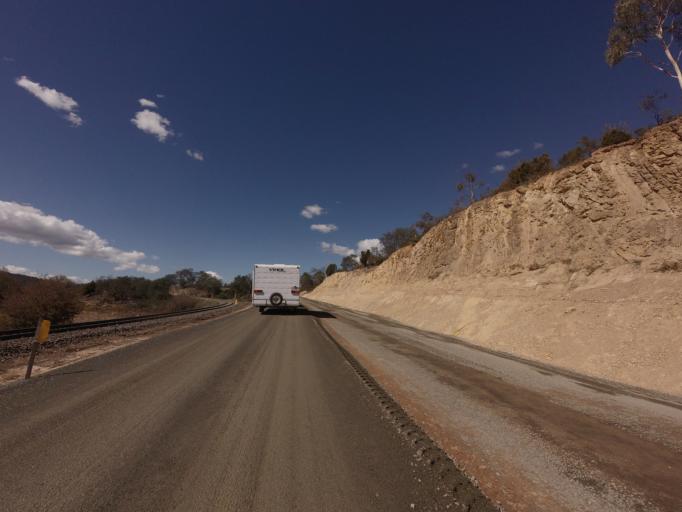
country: AU
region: Tasmania
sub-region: Break O'Day
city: St Helens
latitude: -41.6503
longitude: 147.9314
